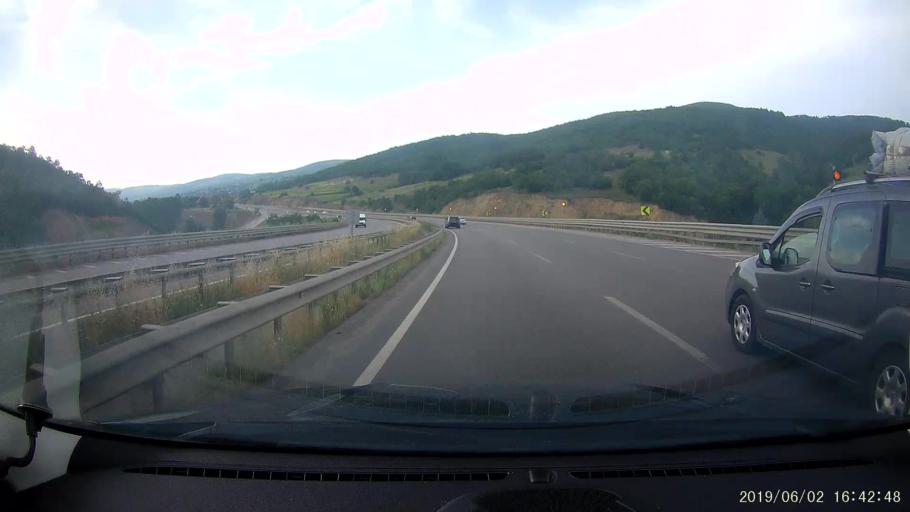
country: TR
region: Samsun
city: Kavak
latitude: 41.1238
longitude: 36.1378
